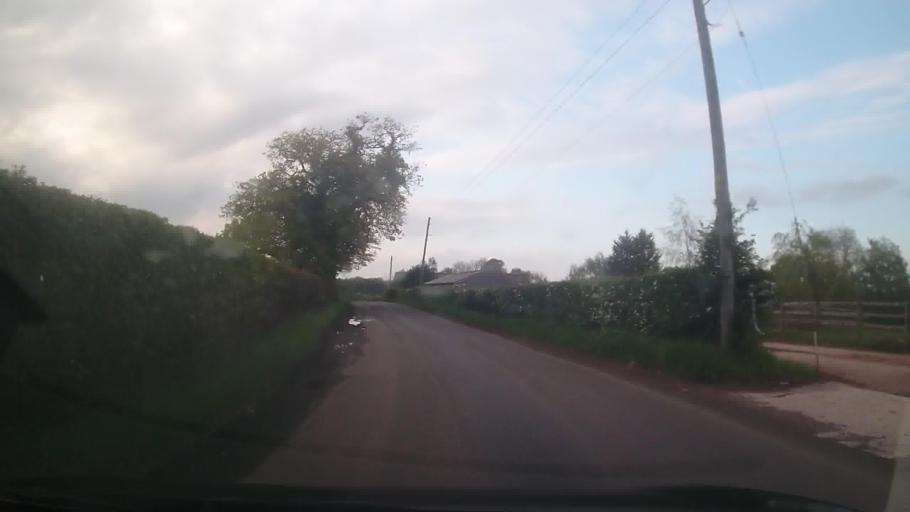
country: GB
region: England
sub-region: Shropshire
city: Ellesmere
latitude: 52.9413
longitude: -2.8729
